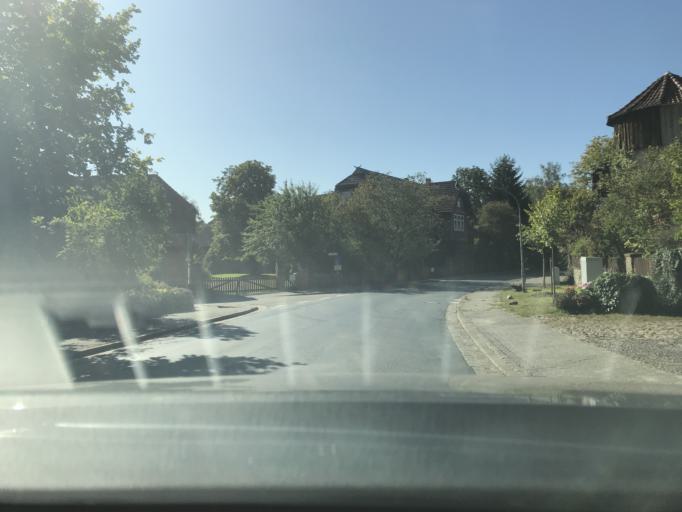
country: DE
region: Lower Saxony
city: Gerdau
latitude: 52.9671
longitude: 10.4191
